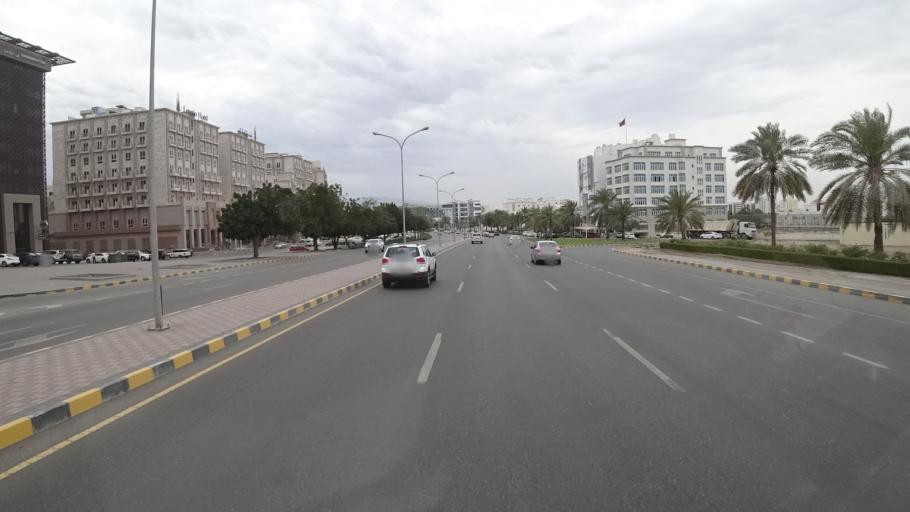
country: OM
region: Muhafazat Masqat
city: Bawshar
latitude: 23.5852
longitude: 58.4100
